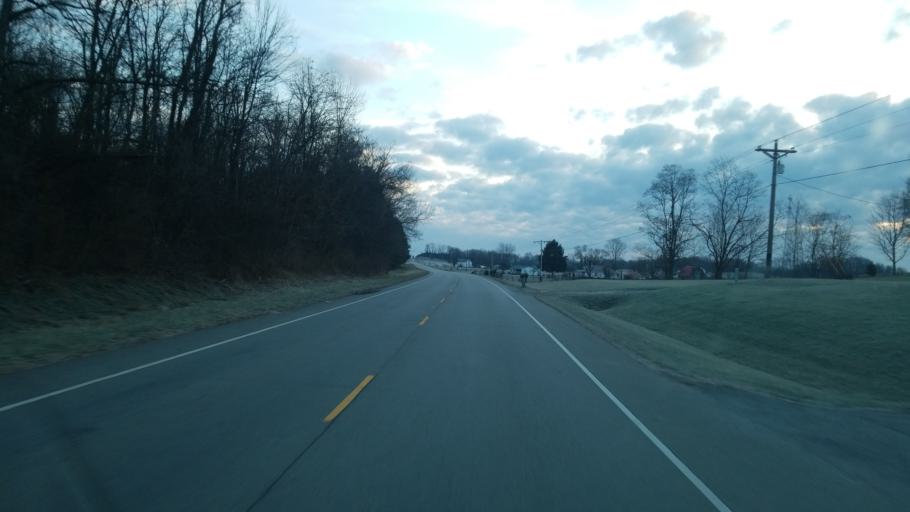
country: US
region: Ohio
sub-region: Highland County
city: Greenfield
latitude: 39.2281
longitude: -83.3774
